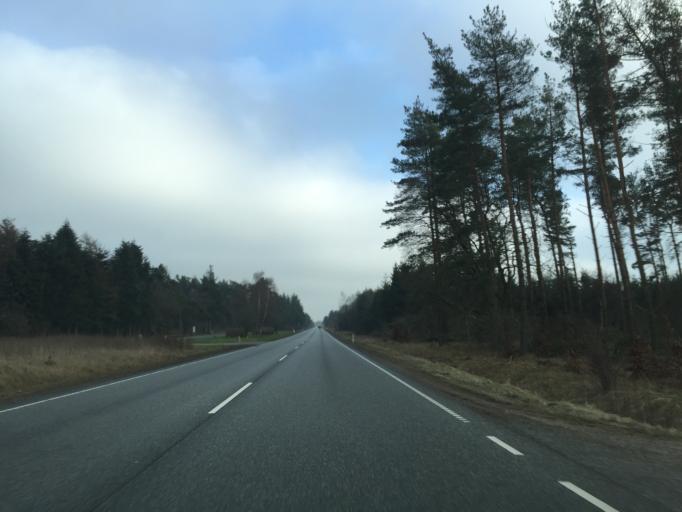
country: DK
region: Central Jutland
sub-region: Viborg Kommune
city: Bjerringbro
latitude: 56.2824
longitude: 9.7015
